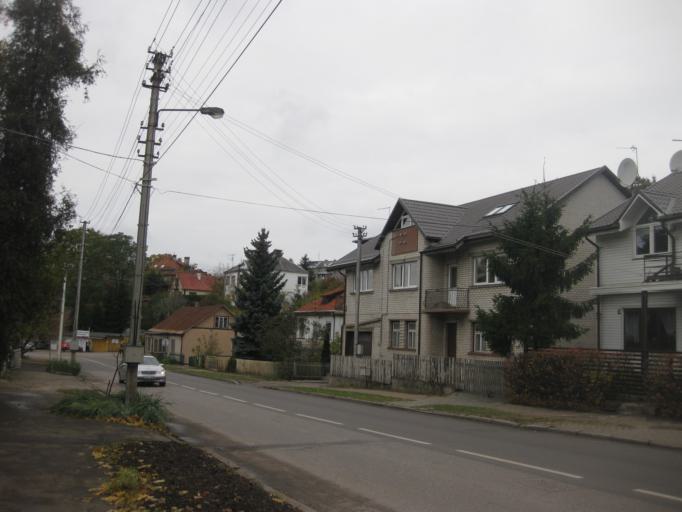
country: LT
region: Kauno apskritis
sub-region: Kaunas
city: Kaunas
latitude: 54.9055
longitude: 23.9165
